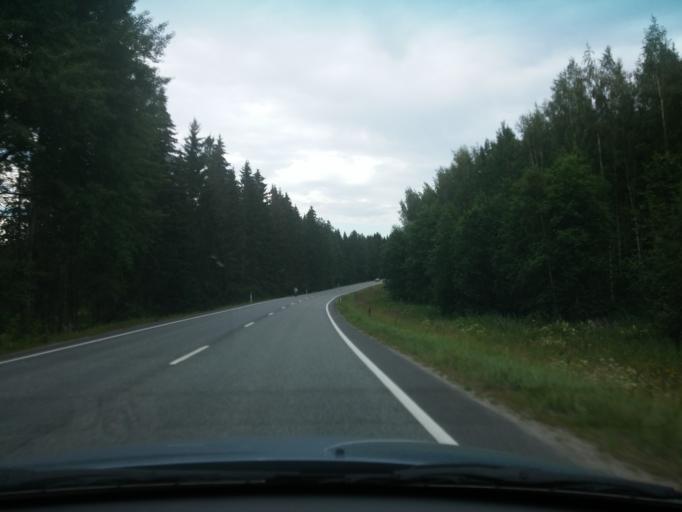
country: FI
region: Haeme
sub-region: Haemeenlinna
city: Tervakoski
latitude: 60.7450
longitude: 24.6591
